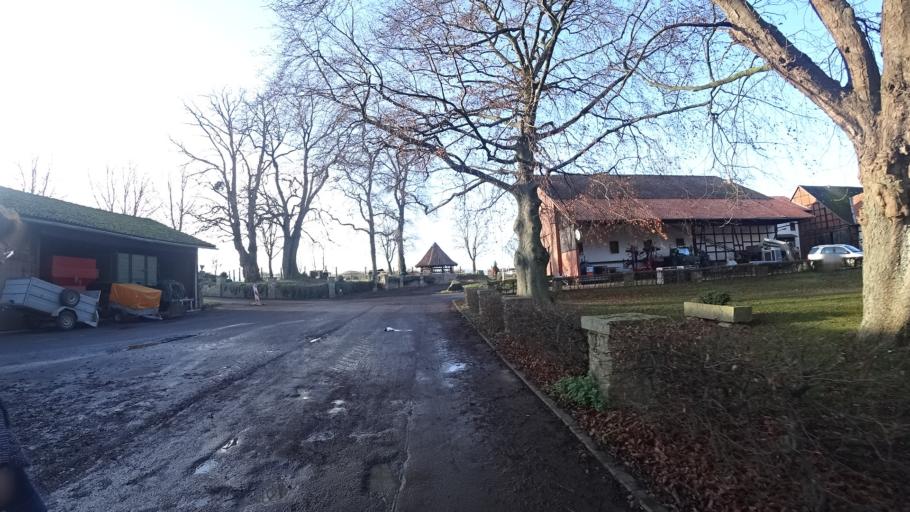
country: DE
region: Lower Saxony
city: Lauenau
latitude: 52.2822
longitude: 9.3568
